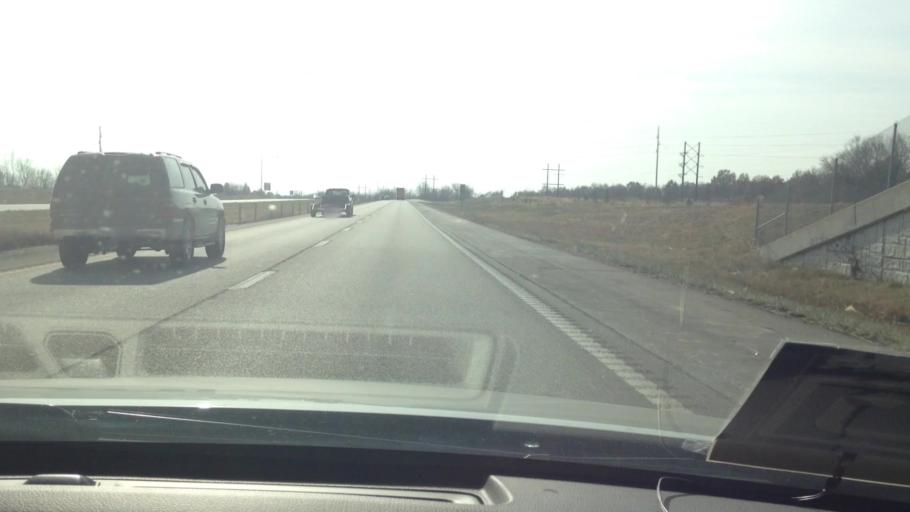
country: US
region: Missouri
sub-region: Cass County
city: Belton
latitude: 38.7858
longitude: -94.4978
